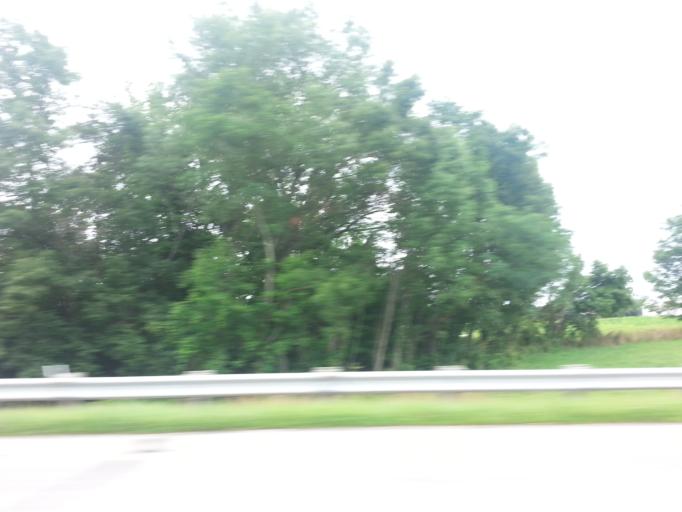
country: US
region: Ohio
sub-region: Brown County
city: Ripley
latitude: 38.8274
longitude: -83.8279
